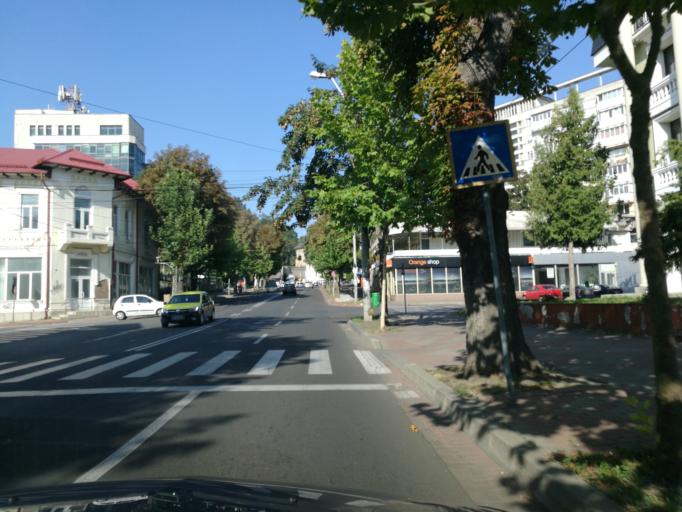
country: RO
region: Neamt
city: Piatra Neamt
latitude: 46.9312
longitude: 26.3663
